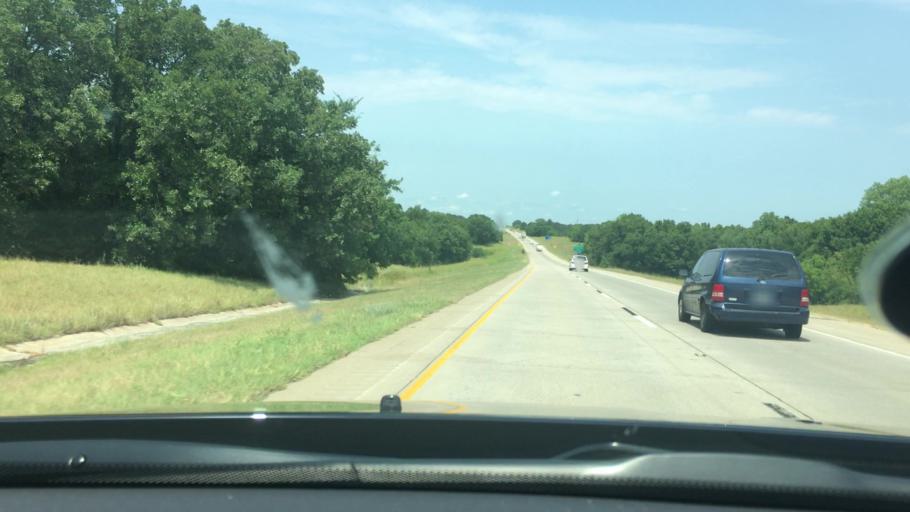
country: US
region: Oklahoma
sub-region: Love County
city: Marietta
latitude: 34.0048
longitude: -97.1415
